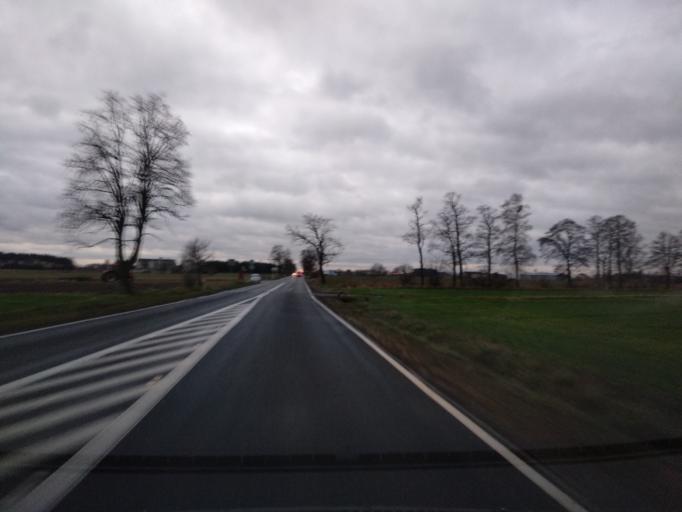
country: PL
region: Greater Poland Voivodeship
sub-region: Powiat koninski
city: Stare Miasto
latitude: 52.1468
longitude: 18.1985
